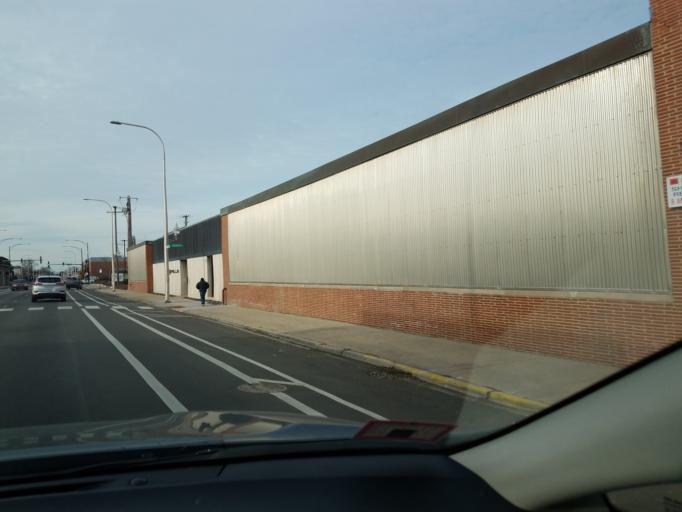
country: US
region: Illinois
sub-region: Cook County
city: Lincolnwood
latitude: 41.9780
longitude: -87.7560
